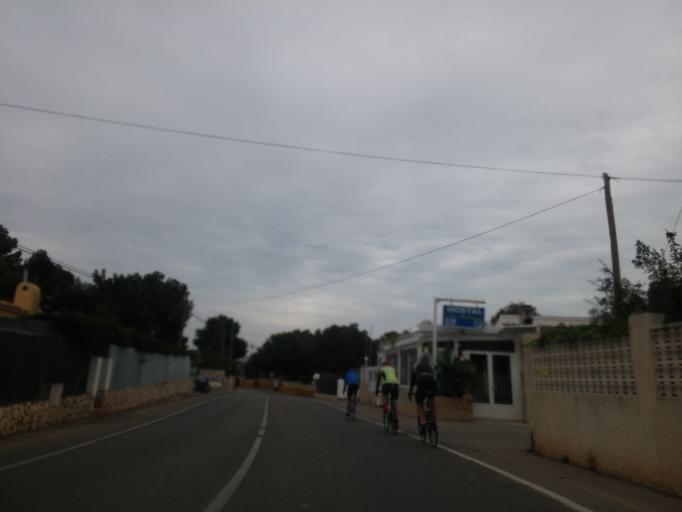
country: ES
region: Valencia
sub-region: Provincia de Alicante
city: Calp
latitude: 38.6568
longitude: 0.0773
